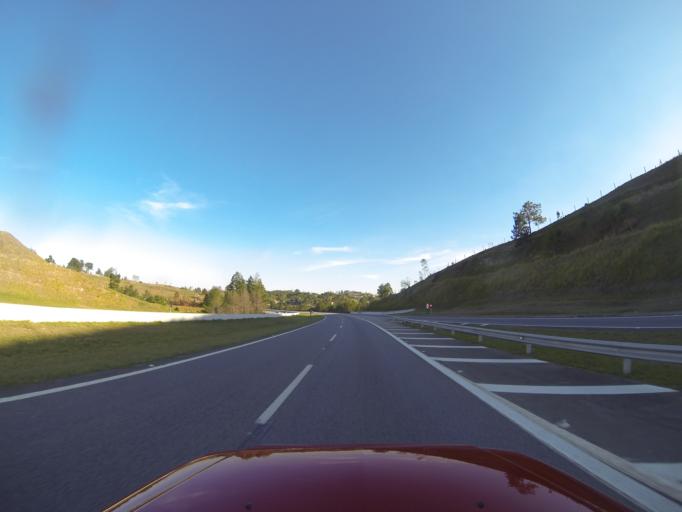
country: BR
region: Sao Paulo
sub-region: Jacarei
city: Jacarei
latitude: -23.3124
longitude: -46.0457
